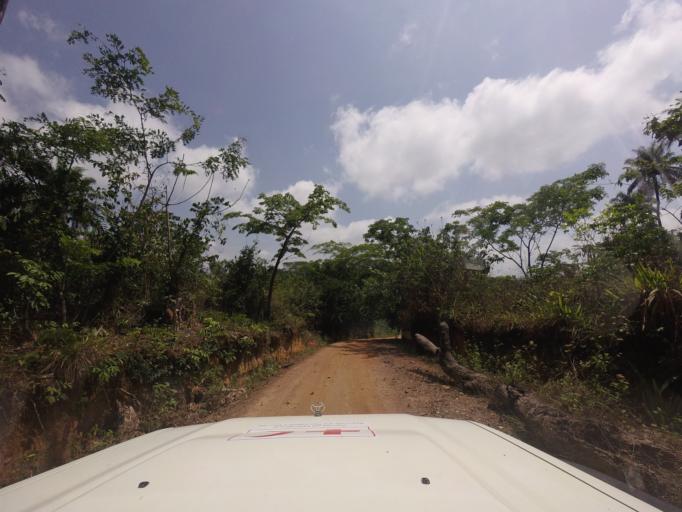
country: LR
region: Lofa
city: Voinjama
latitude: 8.4723
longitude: -9.6643
